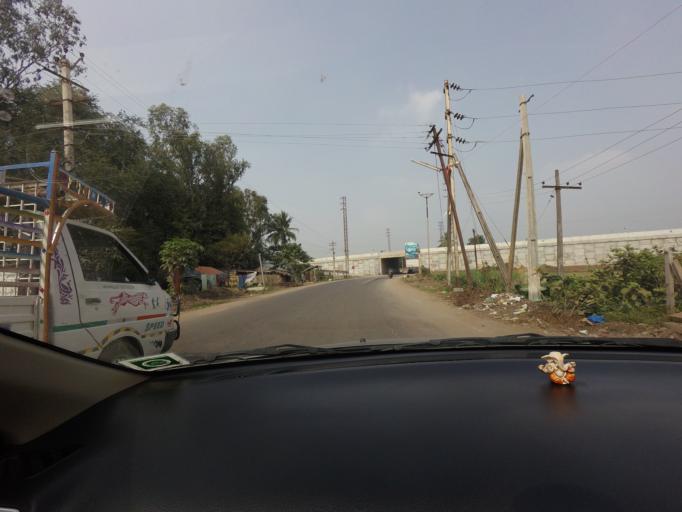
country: IN
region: Andhra Pradesh
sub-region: Krishna
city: Kankipadu
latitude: 16.4397
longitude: 80.7690
